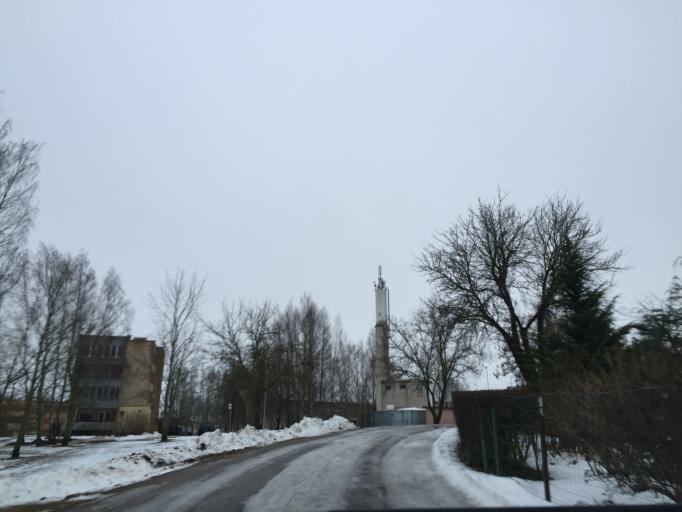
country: LV
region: Krimulda
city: Ragana
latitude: 57.1832
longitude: 24.7029
